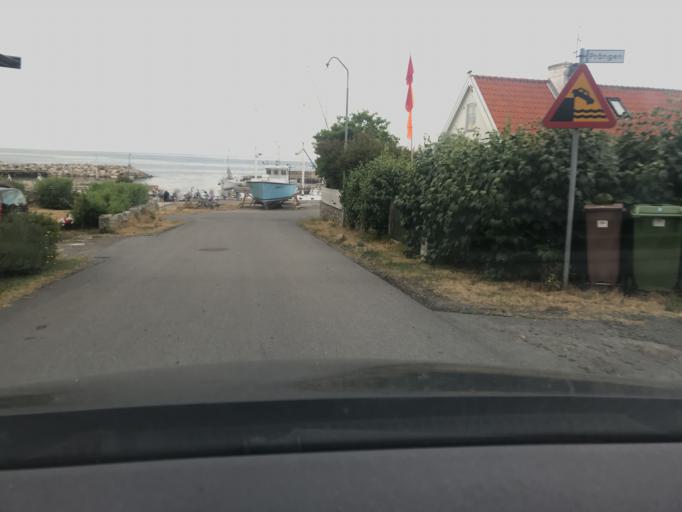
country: SE
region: Skane
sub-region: Simrishamns Kommun
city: Simrishamn
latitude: 55.5930
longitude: 14.3157
